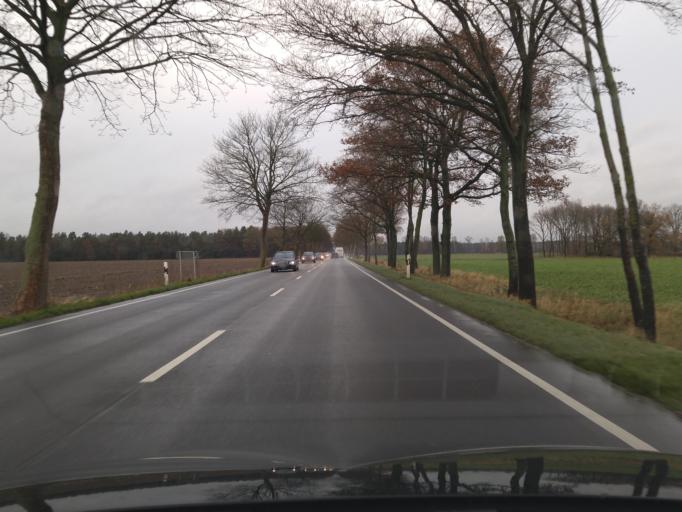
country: DE
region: Lower Saxony
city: Gross Oesingen
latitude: 52.6683
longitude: 10.4677
